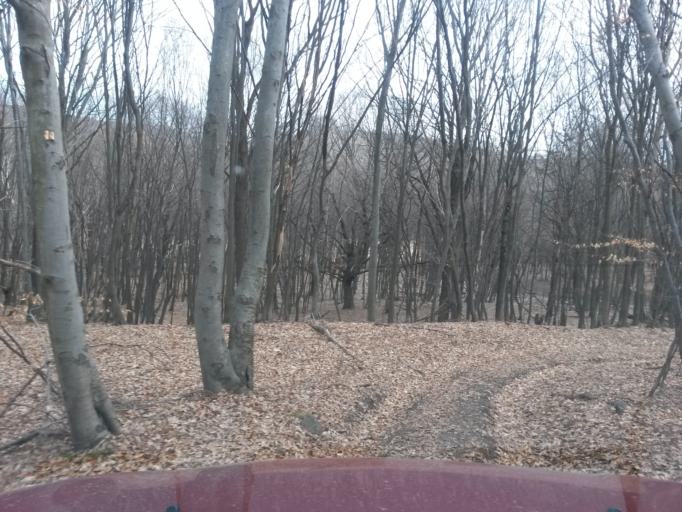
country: HU
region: Borsod-Abauj-Zemplen
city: Gonc
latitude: 48.5756
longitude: 21.3854
